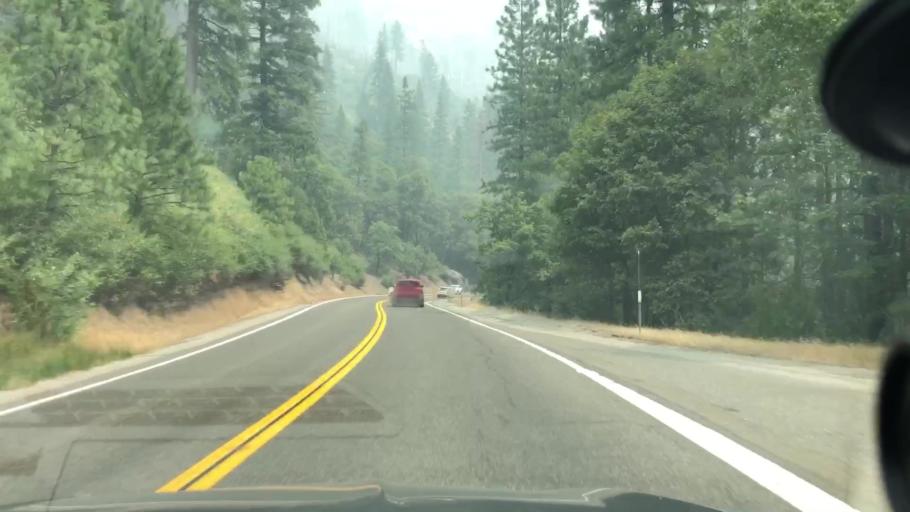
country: US
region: California
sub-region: El Dorado County
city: Pollock Pines
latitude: 38.7753
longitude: -120.2826
